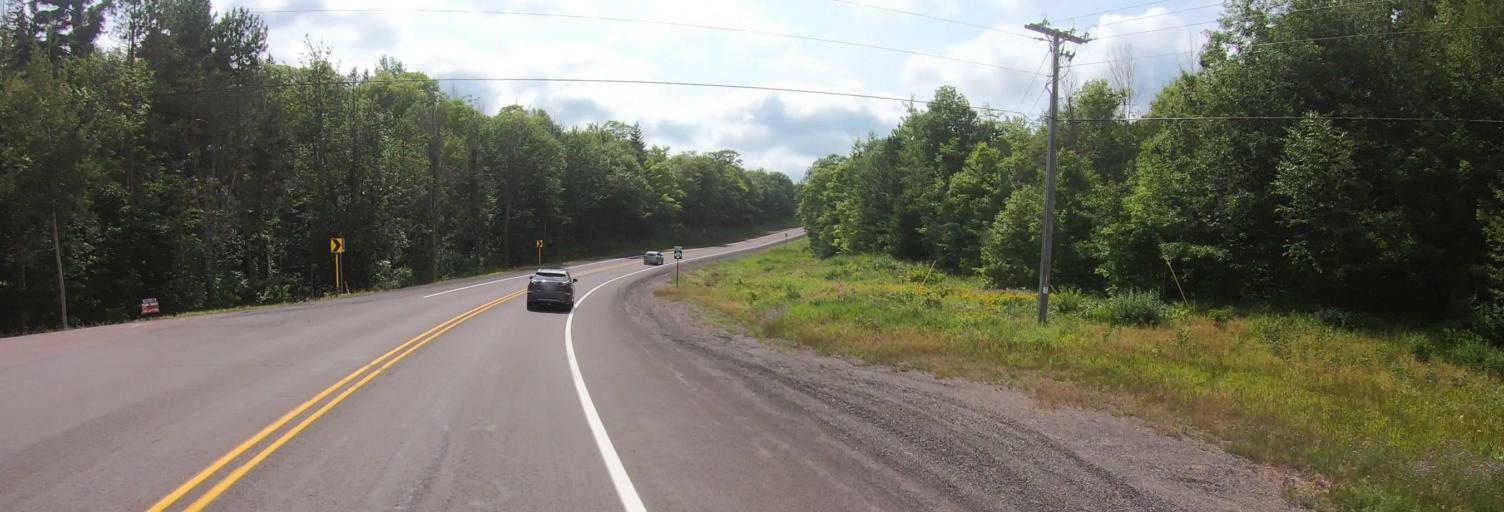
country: US
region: Michigan
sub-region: Houghton County
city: Hancock
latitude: 47.0388
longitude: -88.6736
